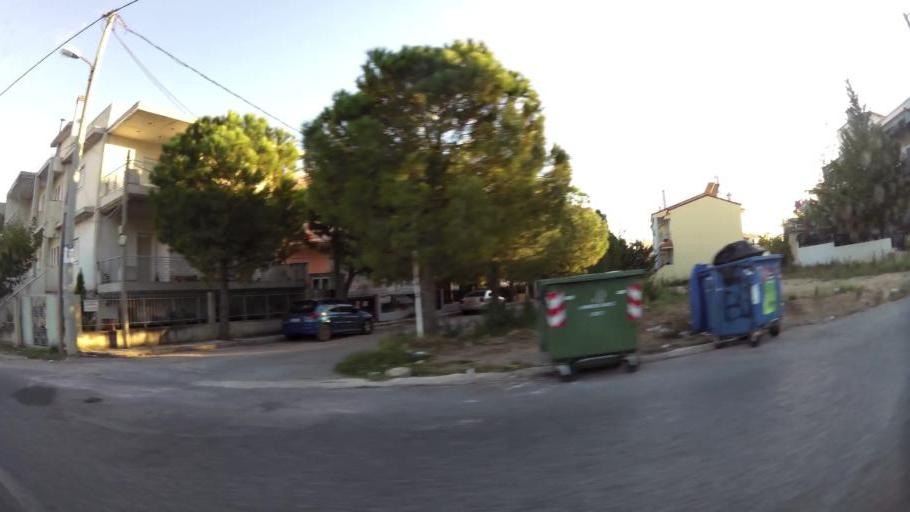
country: GR
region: Attica
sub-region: Nomarchia Dytikis Attikis
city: Ano Liosia
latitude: 38.0894
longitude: 23.6975
